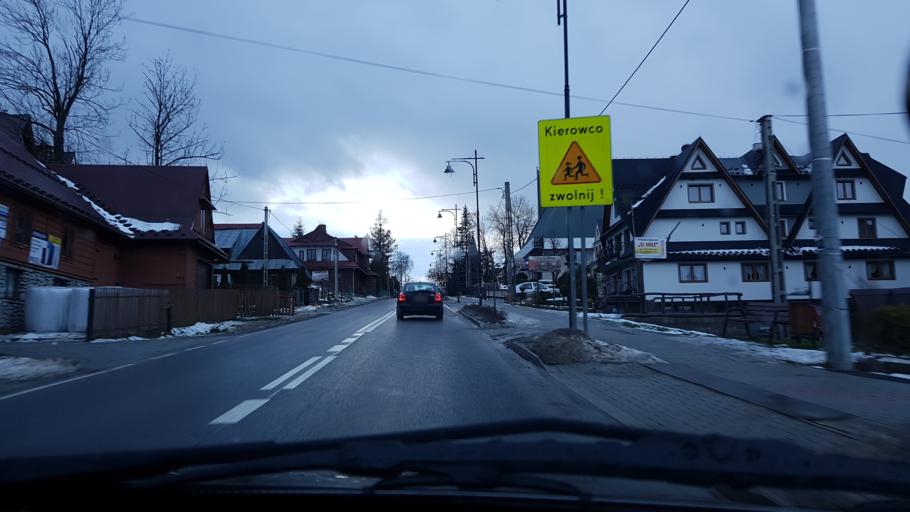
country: PL
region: Lesser Poland Voivodeship
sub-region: Powiat tatrzanski
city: Bukowina Tatrzanska
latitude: 49.3433
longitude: 20.1108
